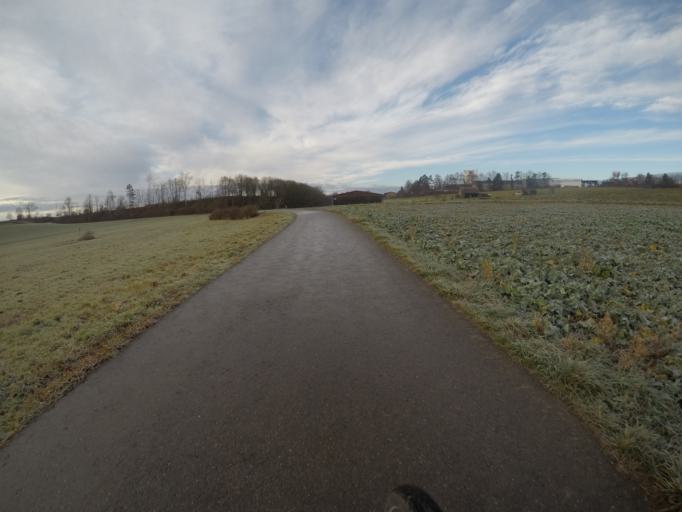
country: DE
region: Baden-Wuerttemberg
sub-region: Regierungsbezirk Stuttgart
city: Magstadt
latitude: 48.7029
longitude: 8.9527
